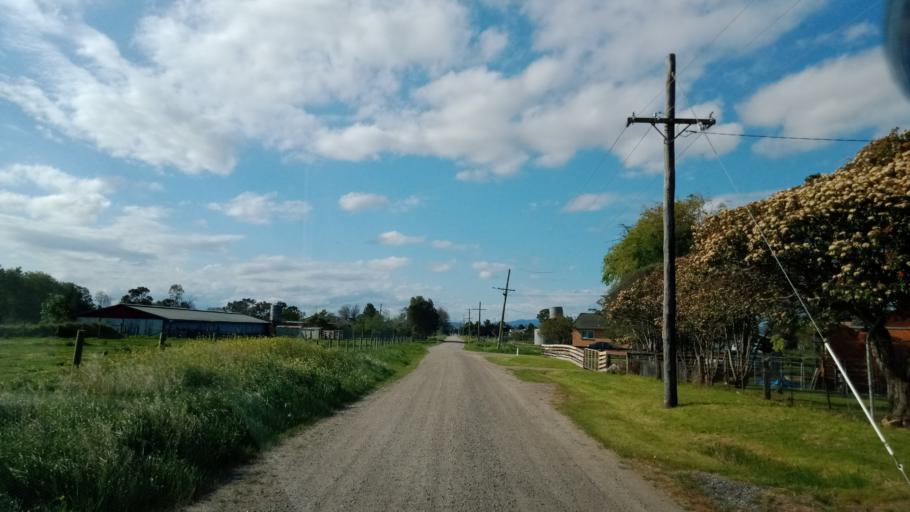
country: AU
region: Victoria
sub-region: Casey
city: Cranbourne West
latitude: -38.0849
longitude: 145.2500
